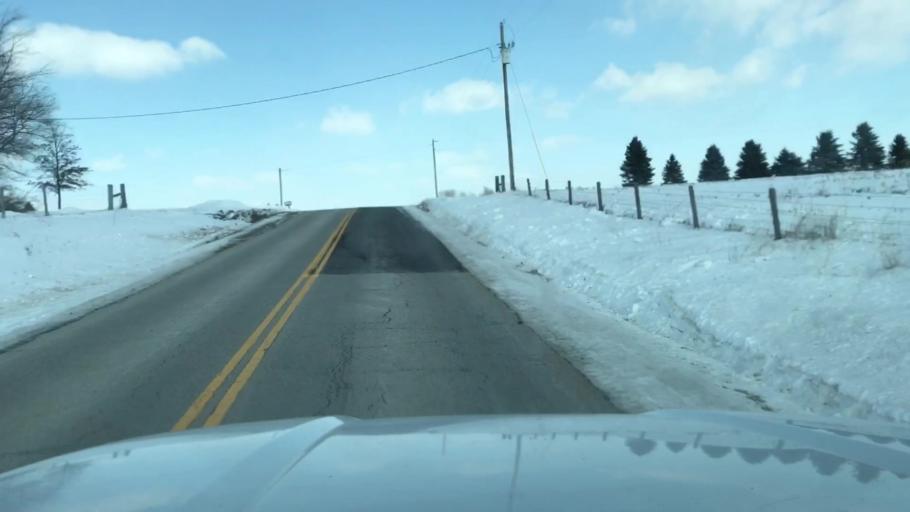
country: US
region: Missouri
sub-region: Nodaway County
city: Maryville
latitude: 40.3618
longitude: -94.7219
